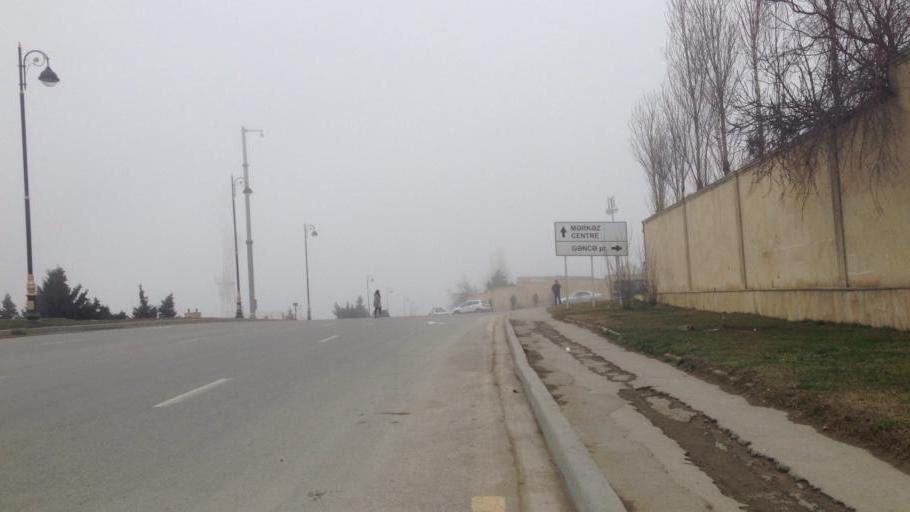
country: AZ
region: Baki
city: Qaracuxur
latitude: 40.3493
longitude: 49.9609
